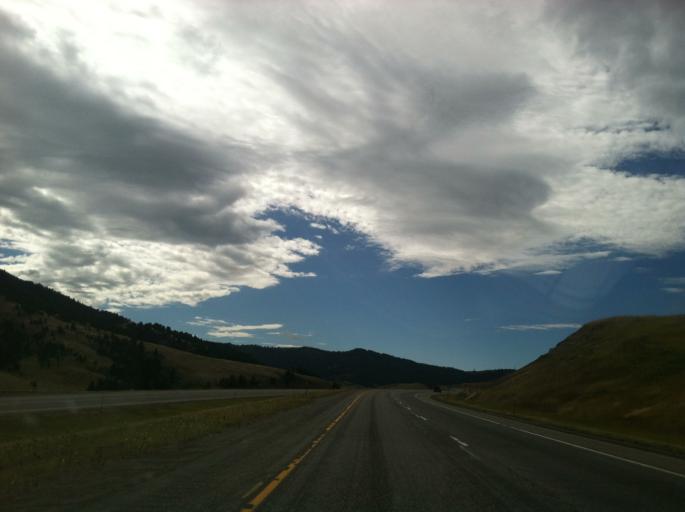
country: US
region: Montana
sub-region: Park County
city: Livingston
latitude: 45.6615
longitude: -110.7313
